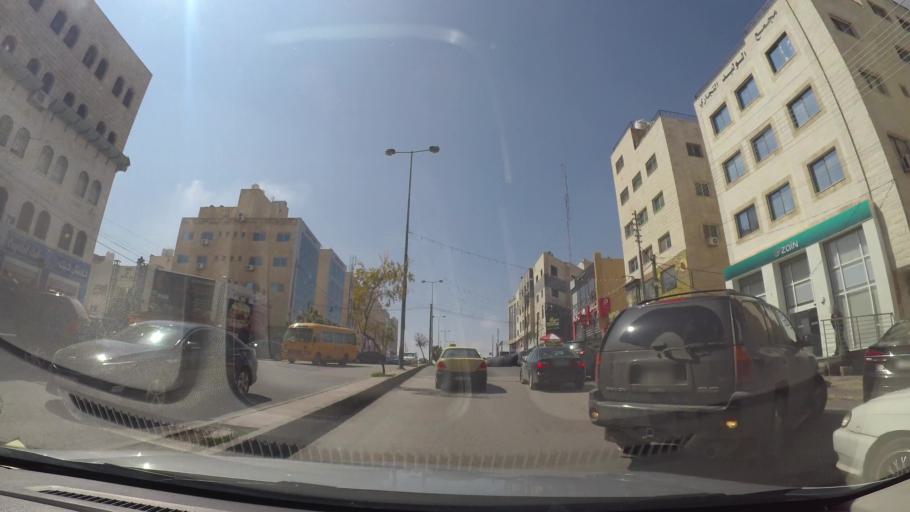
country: JO
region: Amman
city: Al Bunayyat ash Shamaliyah
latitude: 31.9156
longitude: 35.8890
